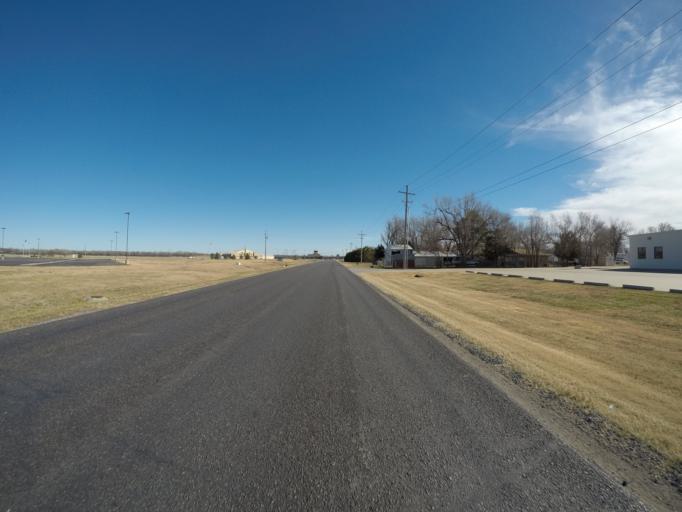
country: US
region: Kansas
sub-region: Reno County
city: Hutchinson
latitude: 38.0649
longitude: -97.8712
